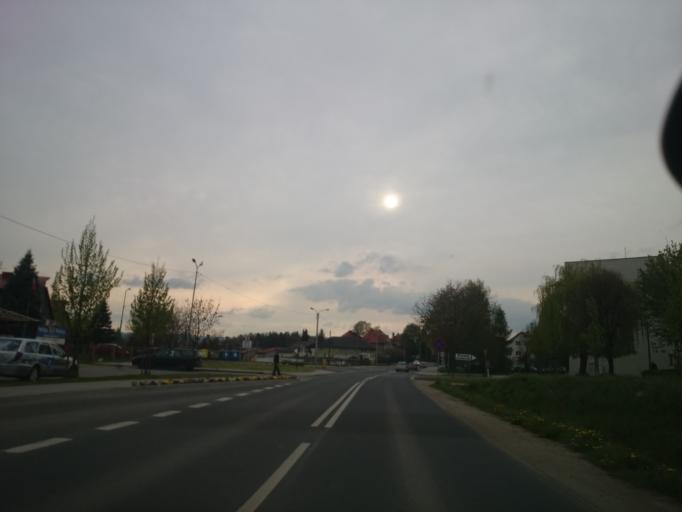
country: PL
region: Lower Silesian Voivodeship
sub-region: Powiat zabkowicki
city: Zabkowice Slaskie
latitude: 50.5877
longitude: 16.8256
